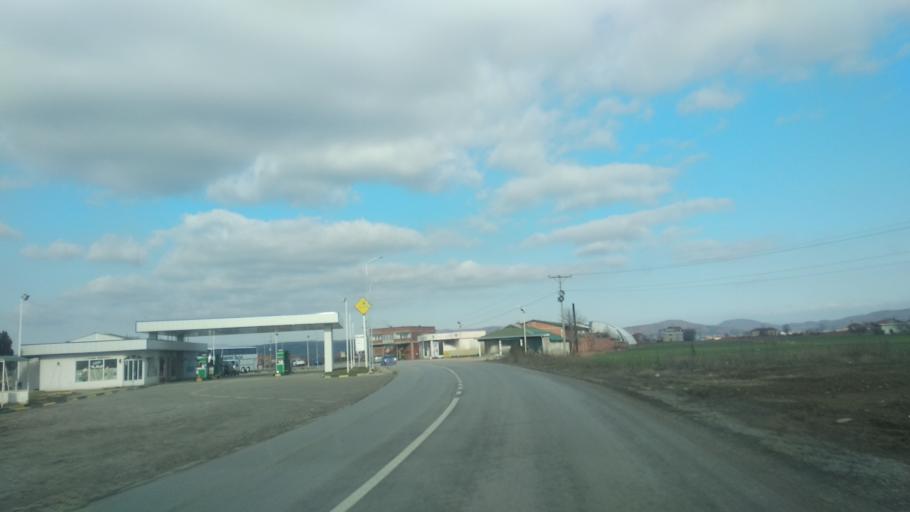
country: XK
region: Pristina
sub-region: Komuna e Obiliqit
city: Obiliq
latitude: 42.7204
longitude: 21.0964
